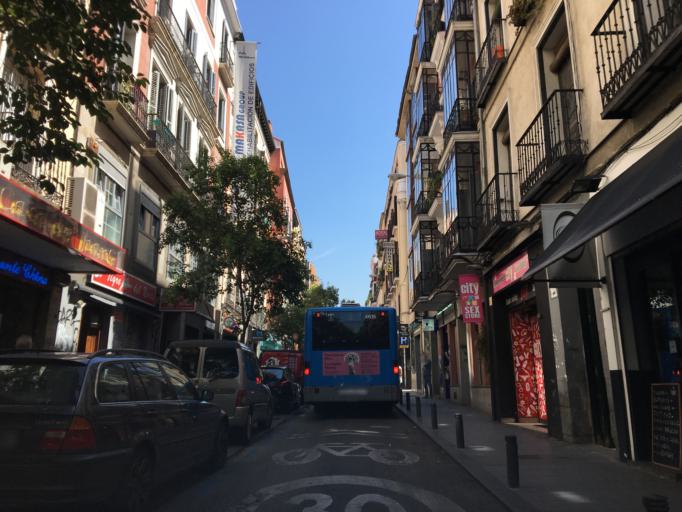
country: ES
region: Madrid
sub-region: Provincia de Madrid
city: City Center
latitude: 40.4215
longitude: -3.7001
